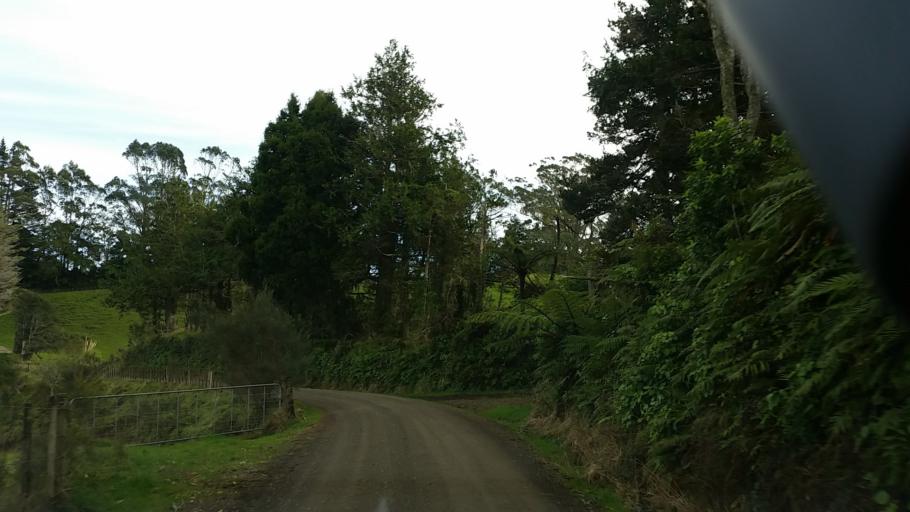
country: NZ
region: Taranaki
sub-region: New Plymouth District
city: Waitara
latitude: -39.0442
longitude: 174.4057
